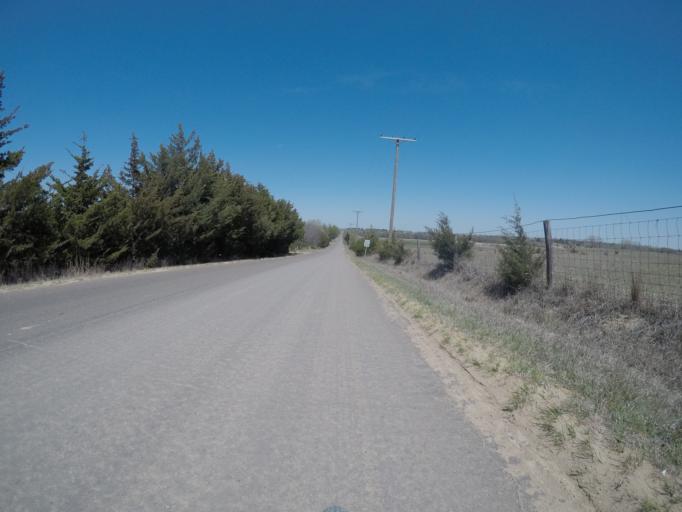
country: US
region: Kansas
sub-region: Pratt County
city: Pratt
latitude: 37.6315
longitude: -98.7670
